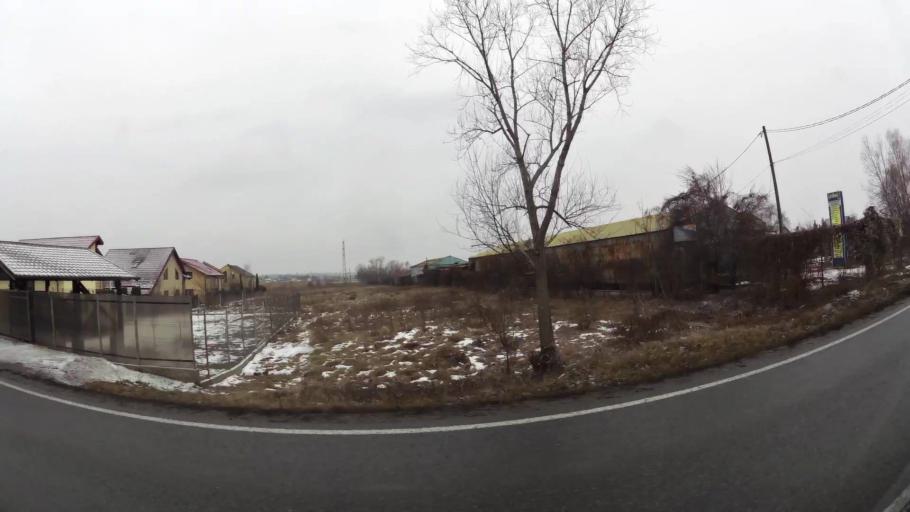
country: RO
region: Dambovita
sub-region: Comuna Aninoasa
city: Viforata
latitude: 44.9505
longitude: 25.4806
